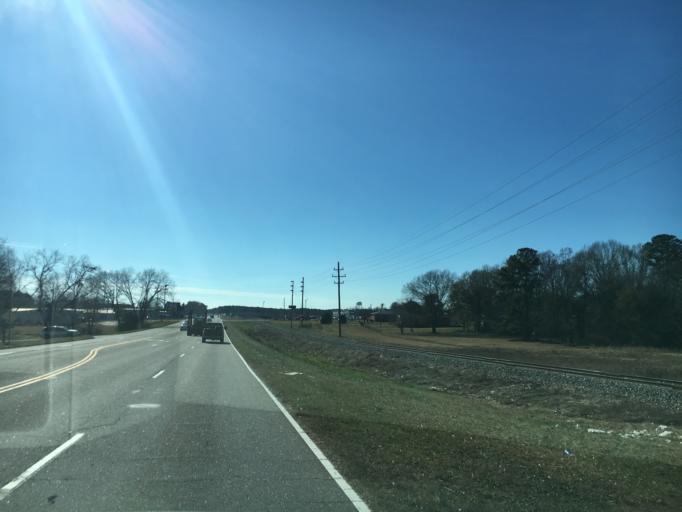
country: US
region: South Carolina
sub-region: Anderson County
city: Homeland Park
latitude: 34.4615
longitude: -82.6629
